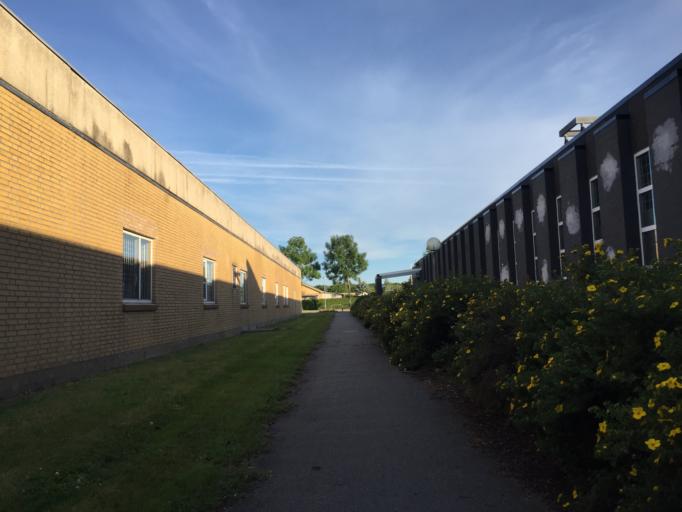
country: DK
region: South Denmark
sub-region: Odense Kommune
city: Neder Holluf
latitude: 55.3784
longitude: 10.4182
